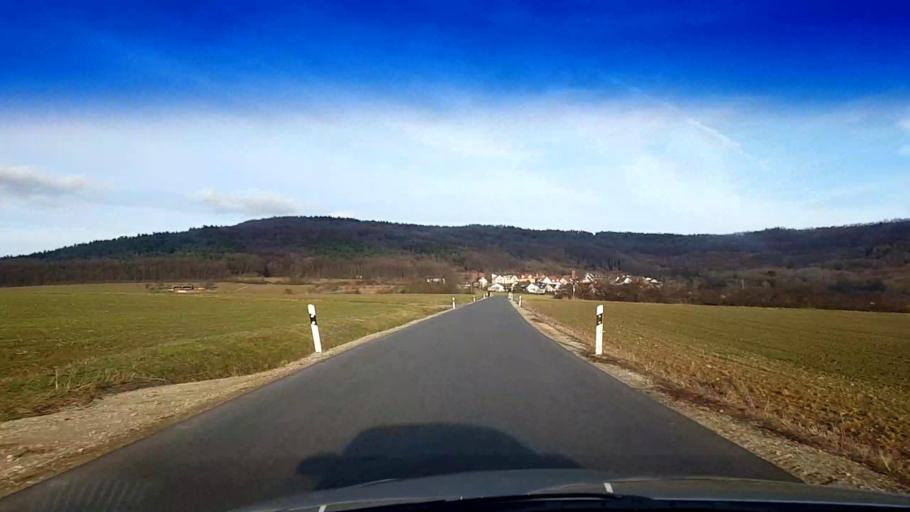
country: DE
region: Bavaria
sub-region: Upper Franconia
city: Buttenheim
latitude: 49.8373
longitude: 11.0245
